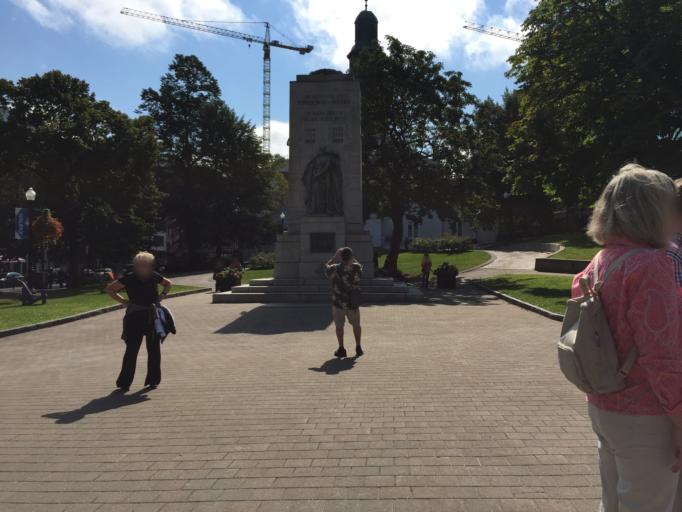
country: CA
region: Nova Scotia
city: Halifax
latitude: 44.6482
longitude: -63.5749
